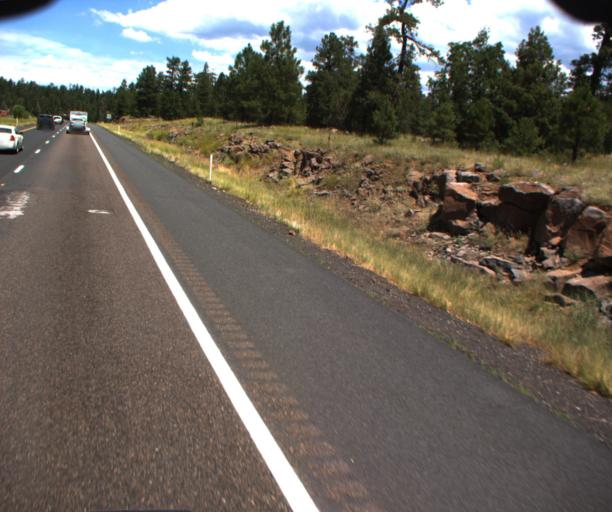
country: US
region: Arizona
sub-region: Coconino County
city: Sedona
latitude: 34.9278
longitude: -111.6474
